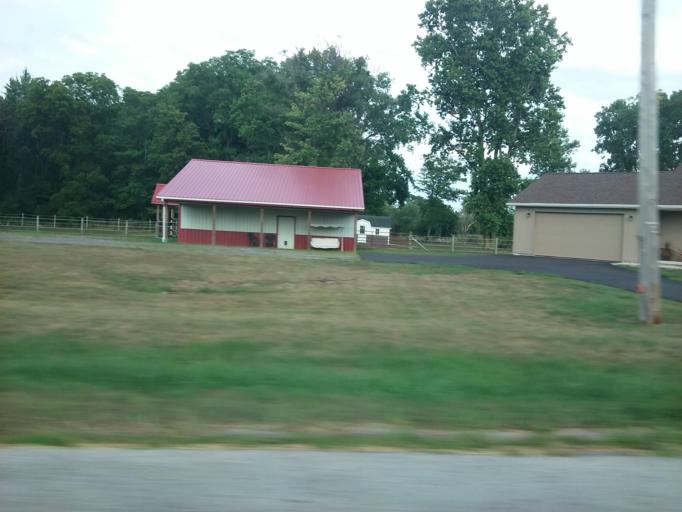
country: US
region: Ohio
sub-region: Wood County
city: Bowling Green
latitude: 41.3005
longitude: -83.6503
